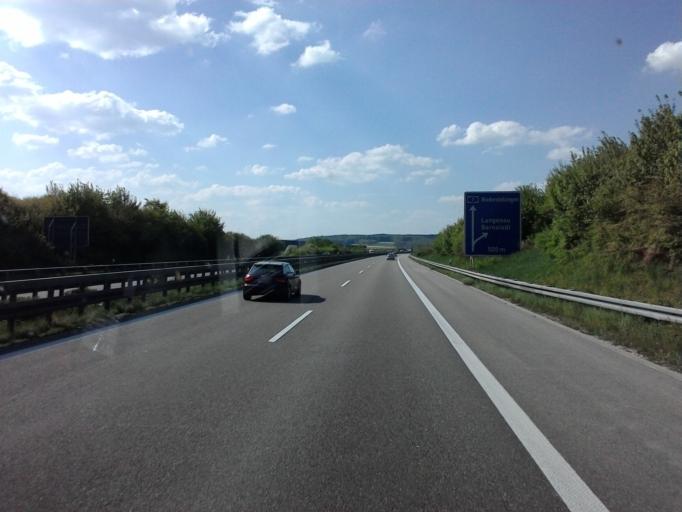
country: DE
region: Baden-Wuerttemberg
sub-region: Tuebingen Region
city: Langenau
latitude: 48.4853
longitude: 10.0969
